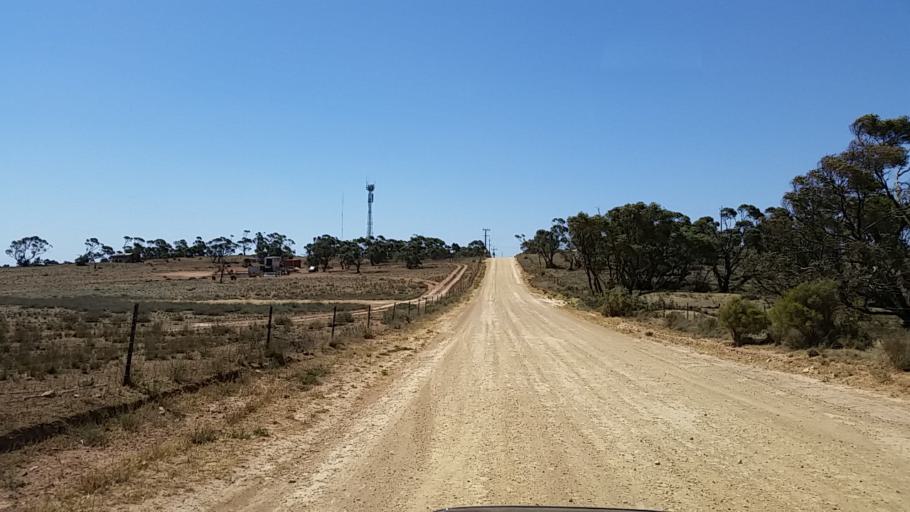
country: AU
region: South Australia
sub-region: Peterborough
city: Peterborough
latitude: -32.9845
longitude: 138.8317
